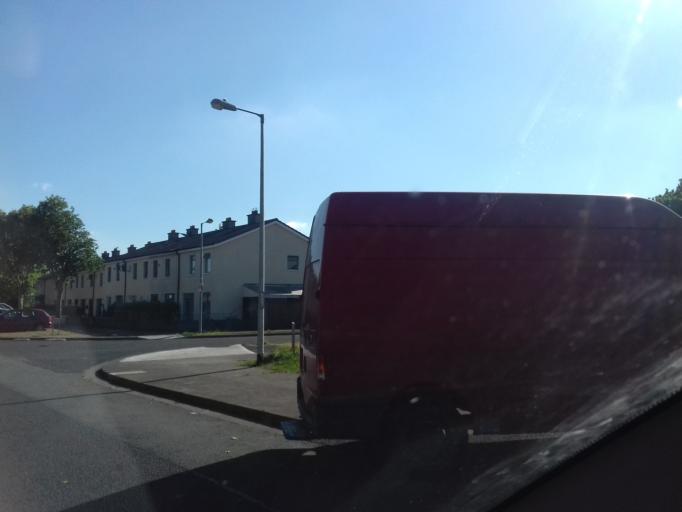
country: IE
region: Leinster
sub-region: Fingal County
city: Blanchardstown
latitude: 53.3964
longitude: -6.3761
